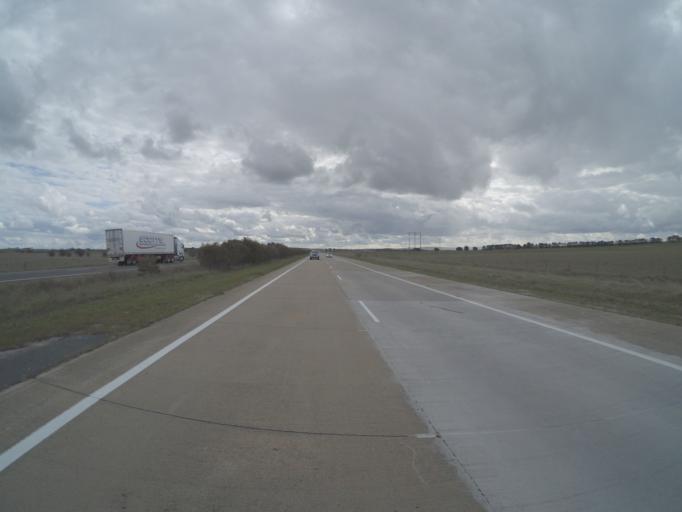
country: AU
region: New South Wales
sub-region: Goulburn Mulwaree
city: Goulburn
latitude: -34.8088
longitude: 149.5787
